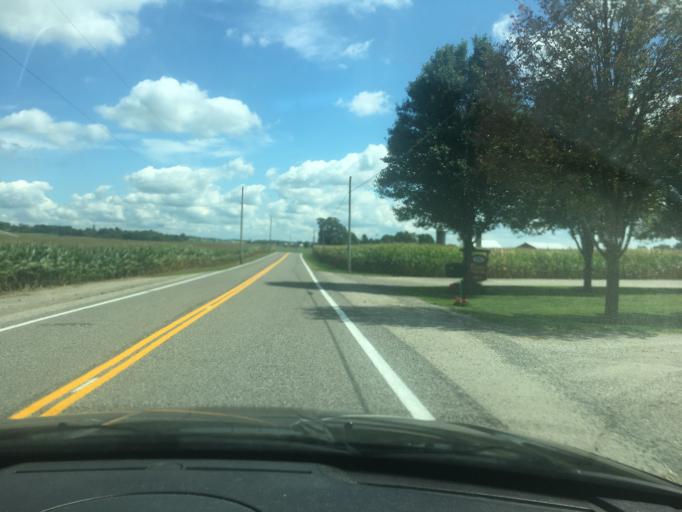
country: US
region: Ohio
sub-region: Logan County
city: West Liberty
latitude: 40.2308
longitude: -83.7132
